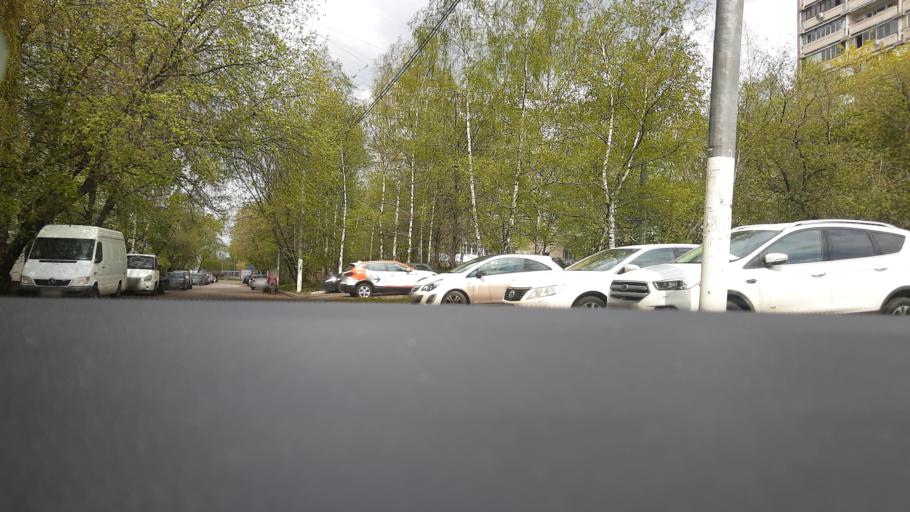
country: RU
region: Moscow
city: Ivanovskoye
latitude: 55.7786
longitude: 37.8259
